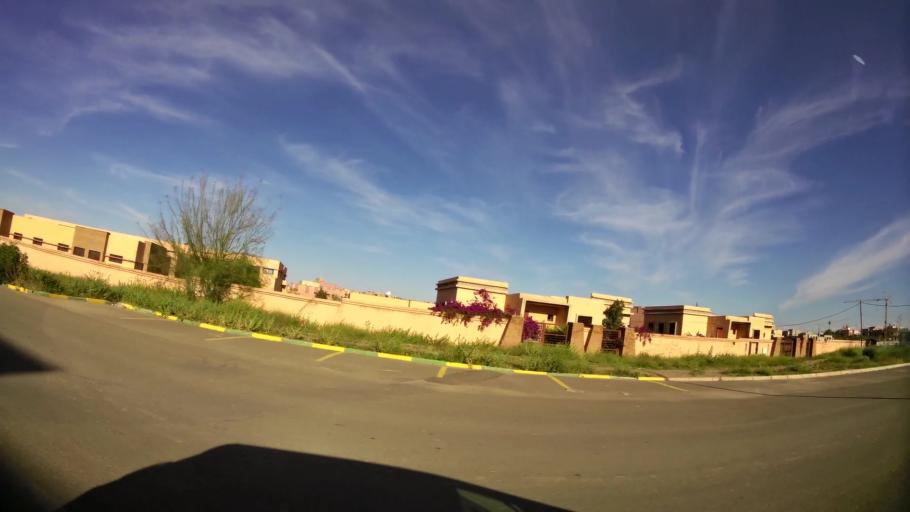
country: MA
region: Marrakech-Tensift-Al Haouz
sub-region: Marrakech
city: Marrakesh
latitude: 31.6803
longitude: -8.0624
